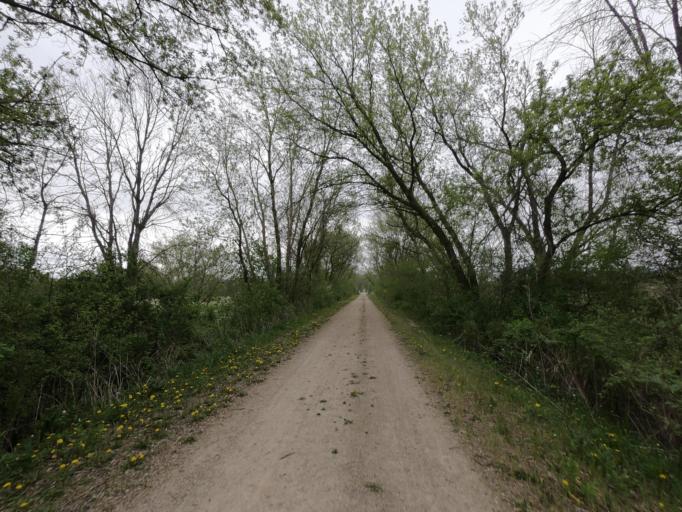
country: US
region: Wisconsin
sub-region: Jefferson County
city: Johnson Creek
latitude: 43.0308
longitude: -88.7465
